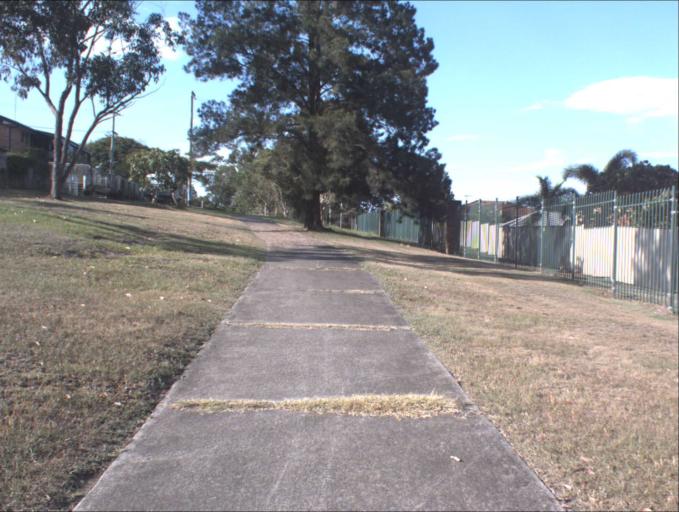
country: AU
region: Queensland
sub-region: Logan
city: Beenleigh
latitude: -27.6790
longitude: 153.2054
